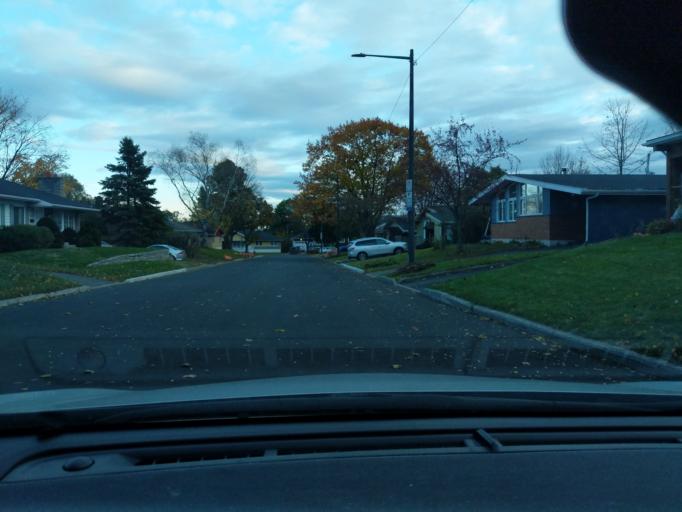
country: CA
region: Quebec
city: L'Ancienne-Lorette
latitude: 46.7644
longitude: -71.2830
